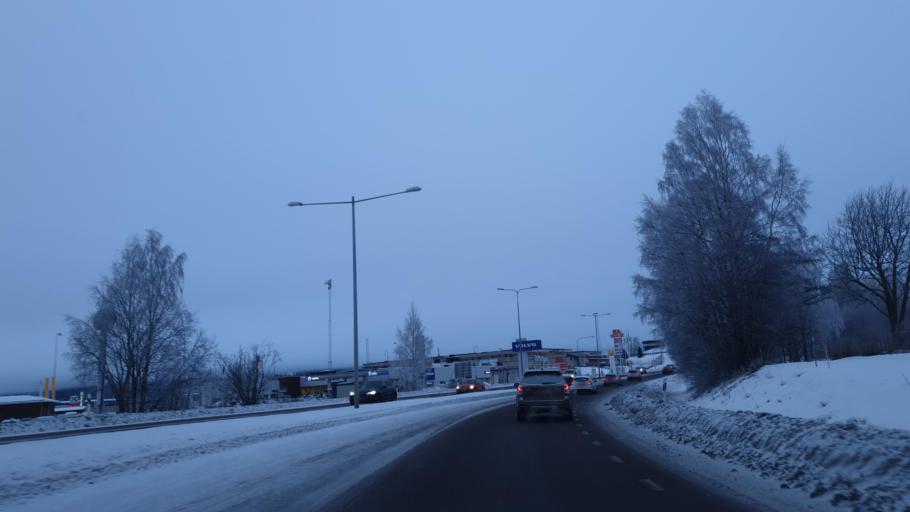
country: SE
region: Vaesternorrland
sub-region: OErnskoeldsviks Kommun
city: Ornskoldsvik
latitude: 63.3006
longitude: 18.7193
